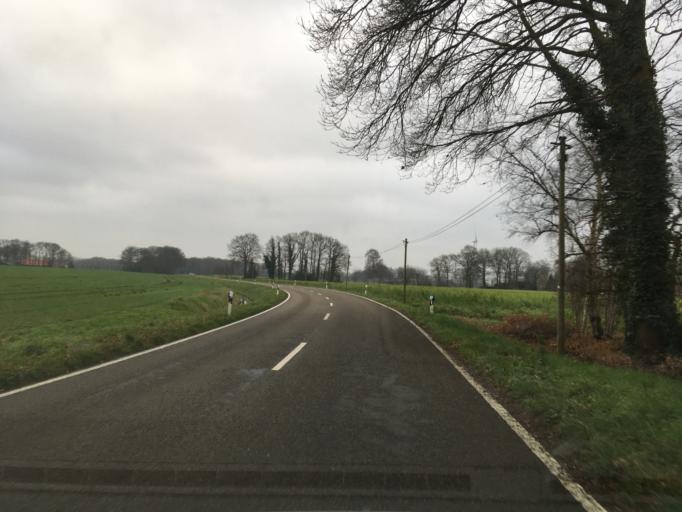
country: DE
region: North Rhine-Westphalia
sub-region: Regierungsbezirk Munster
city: Gronau
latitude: 52.1761
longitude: 7.0761
